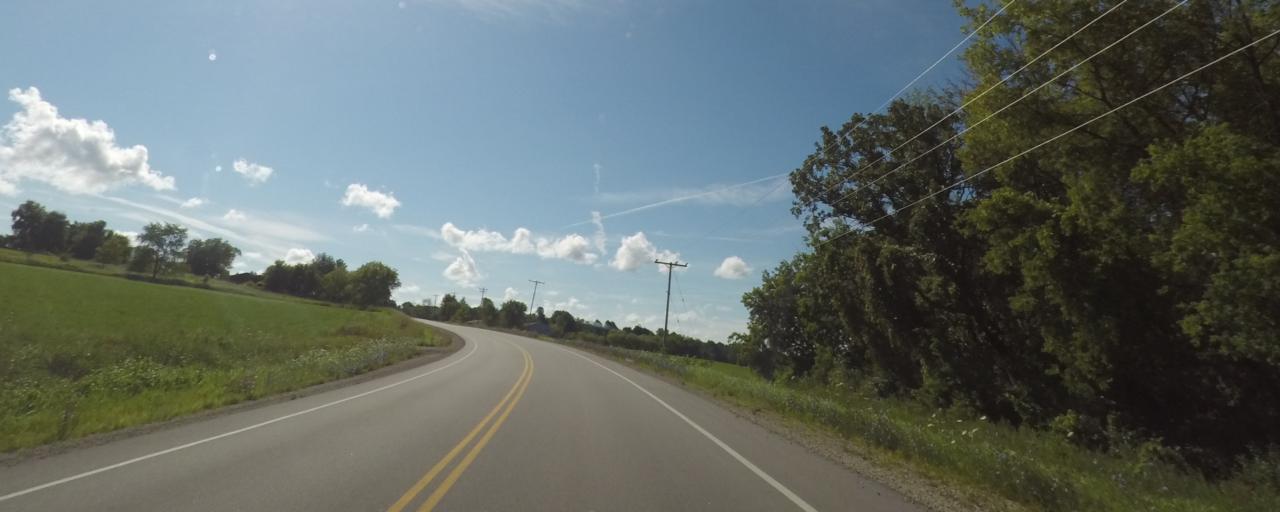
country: US
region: Wisconsin
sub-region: Jefferson County
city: Ixonia
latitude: 43.0700
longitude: -88.6344
